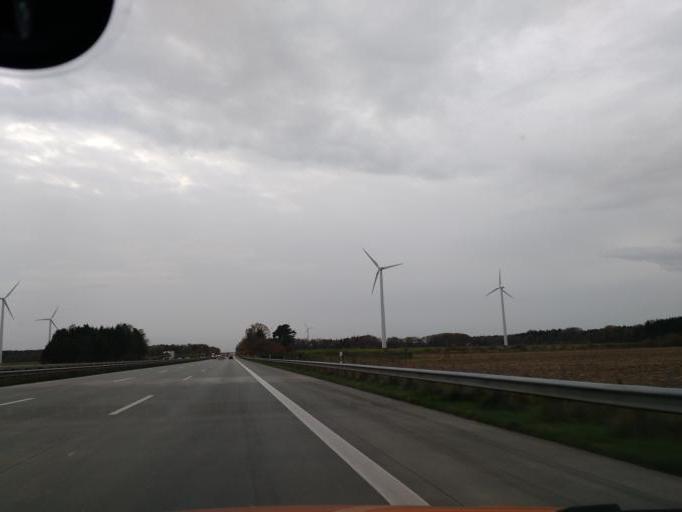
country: DE
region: Lower Saxony
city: Ottersberg
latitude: 53.0764
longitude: 9.1443
